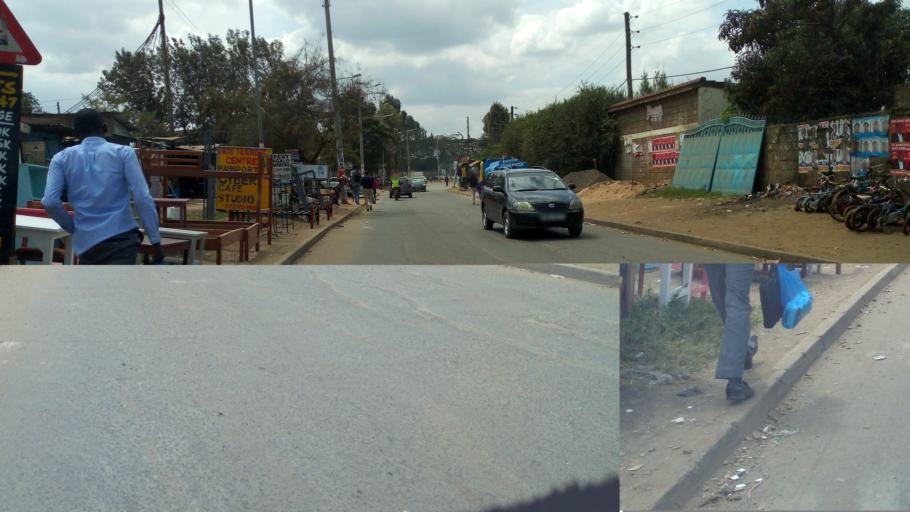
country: KE
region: Nairobi Area
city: Nairobi
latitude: -1.3254
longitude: 36.7854
